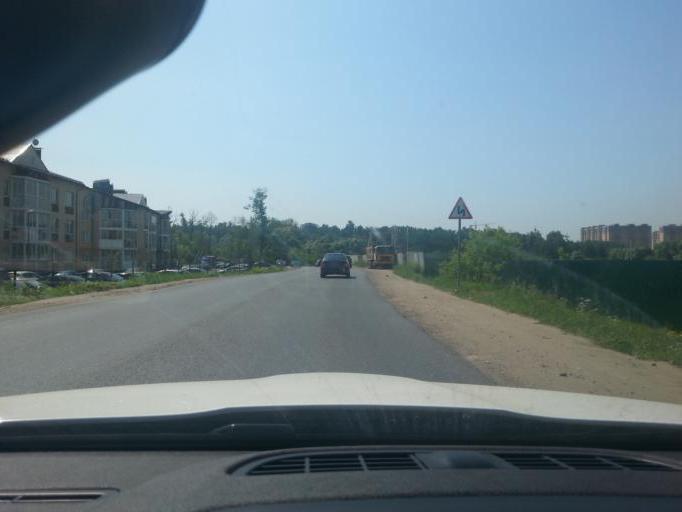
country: RU
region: Moskovskaya
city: Zheleznodorozhnyy
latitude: 55.7133
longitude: 37.9735
